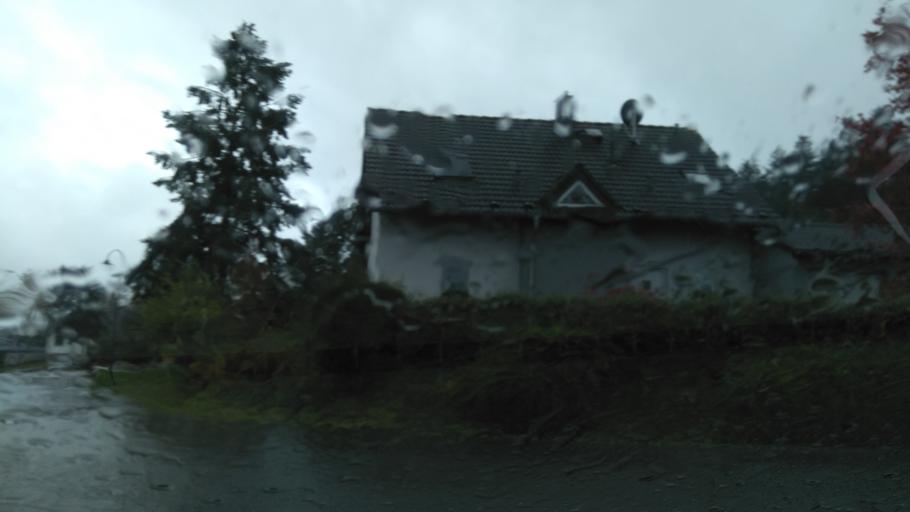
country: DE
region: Rheinland-Pfalz
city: Pellingen
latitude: 49.6763
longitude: 6.6661
